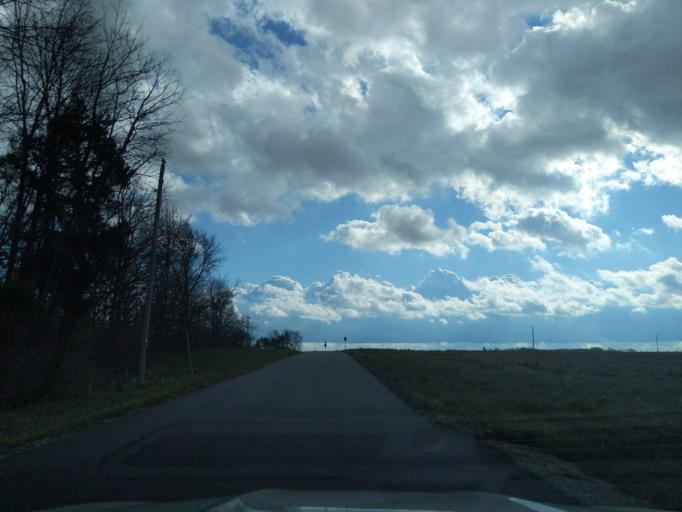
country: US
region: Indiana
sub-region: Decatur County
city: Greensburg
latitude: 39.4103
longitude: -85.5089
